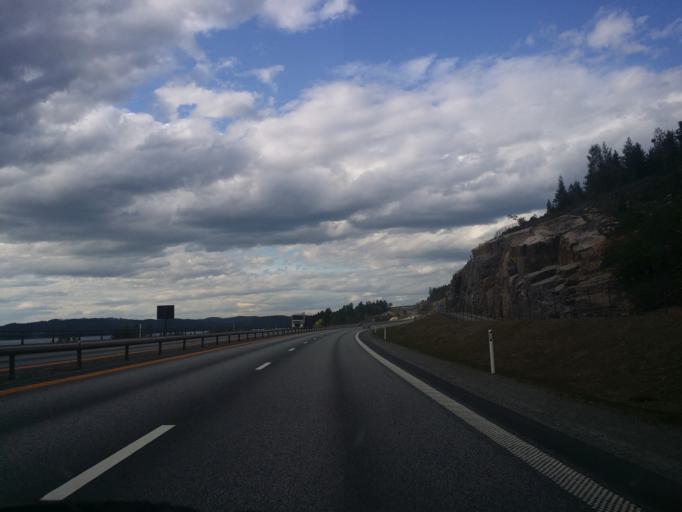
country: NO
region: Hedmark
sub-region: Stange
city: Stange
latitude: 60.5503
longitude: 11.2479
